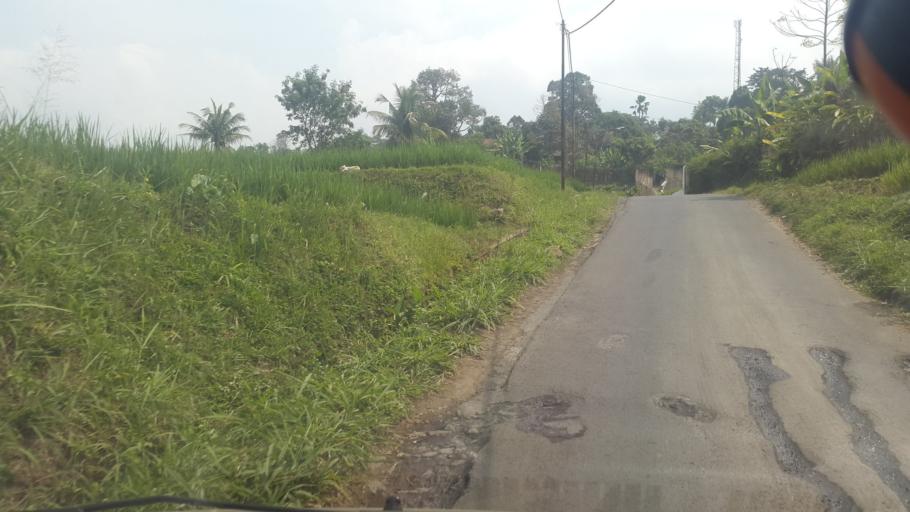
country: ID
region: West Java
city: Cicurug
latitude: -6.7693
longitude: 106.7621
